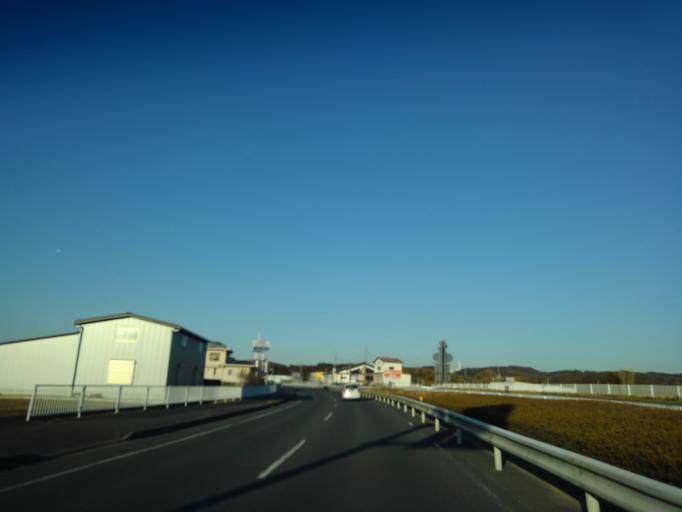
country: JP
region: Chiba
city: Kimitsu
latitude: 35.3125
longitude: 139.9259
